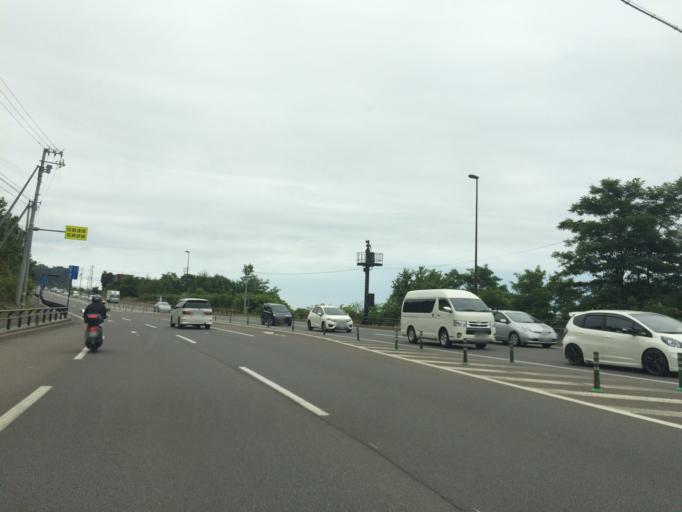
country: JP
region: Hokkaido
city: Otaru
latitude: 43.1512
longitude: 141.1320
